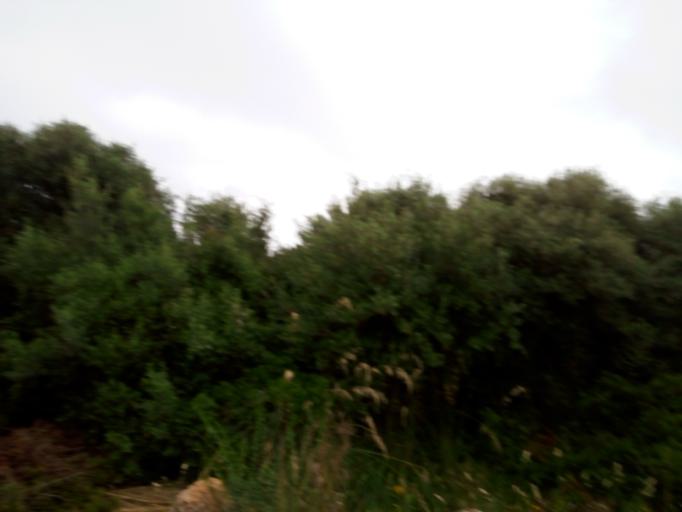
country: DZ
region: Tipaza
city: Tipasa
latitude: 36.5949
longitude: 2.4384
